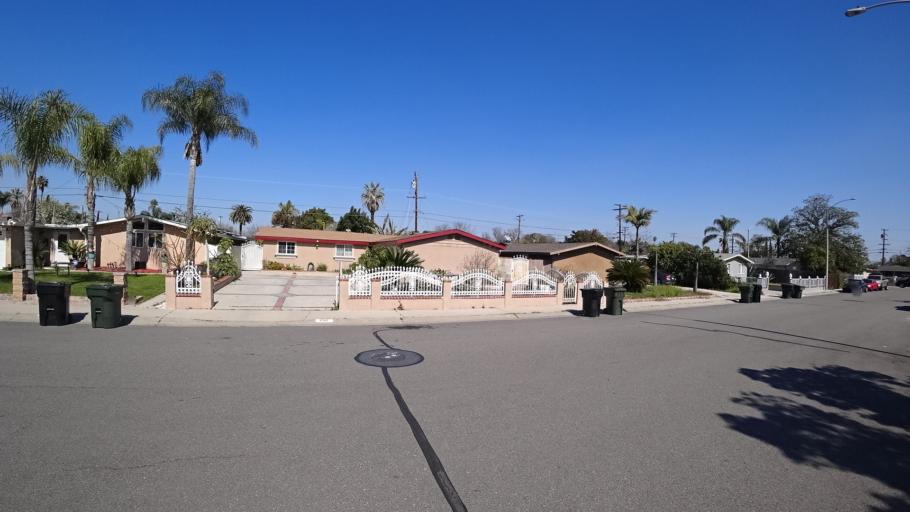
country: US
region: California
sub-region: Orange County
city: Fullerton
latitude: 33.8454
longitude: -117.9560
